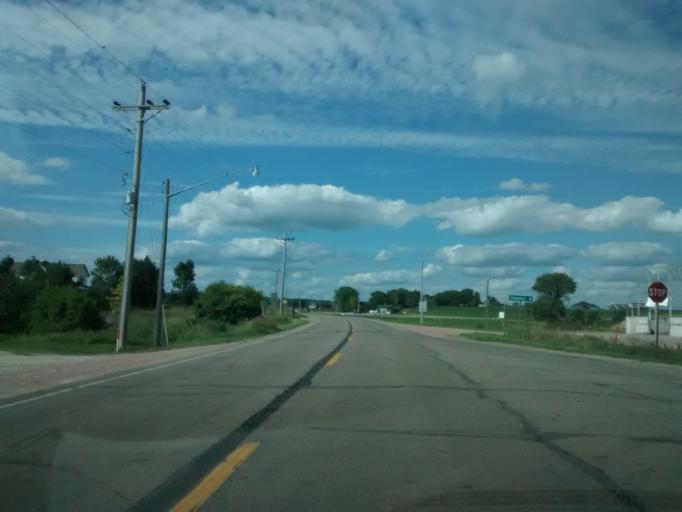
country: US
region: Iowa
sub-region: Woodbury County
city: Moville
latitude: 42.4943
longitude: -96.0725
